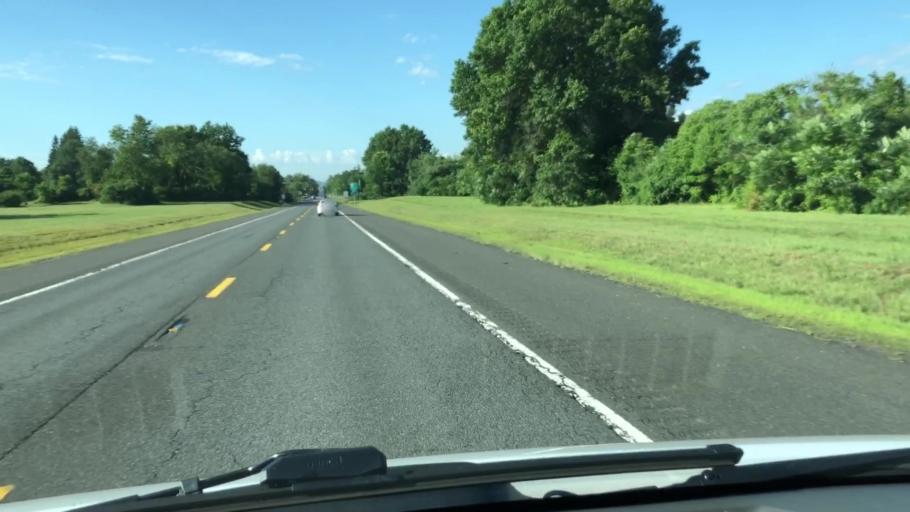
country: US
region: Massachusetts
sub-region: Hampshire County
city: North Amherst
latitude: 42.4134
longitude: -72.5374
